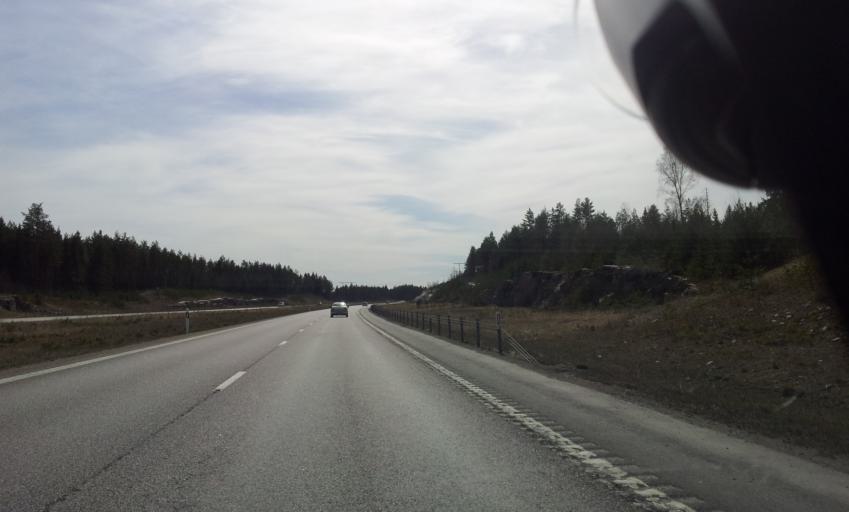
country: SE
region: Uppsala
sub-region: Tierps Kommun
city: Tierp
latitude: 60.3053
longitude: 17.5211
